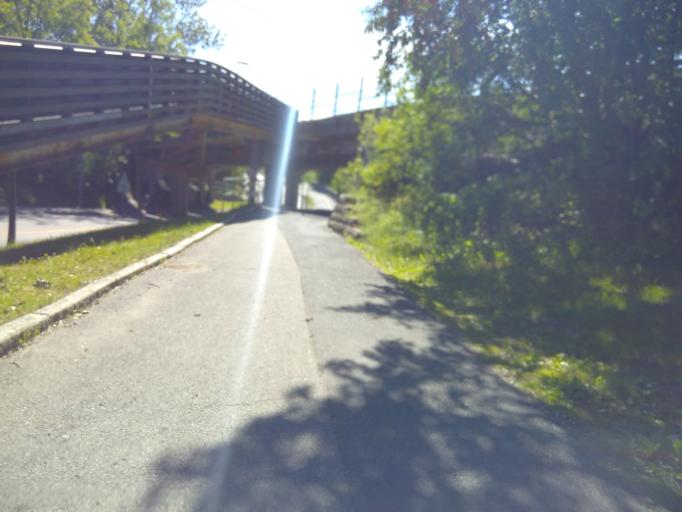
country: NO
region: Akershus
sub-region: Baerum
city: Lysaker
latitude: 59.9463
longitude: 10.6487
